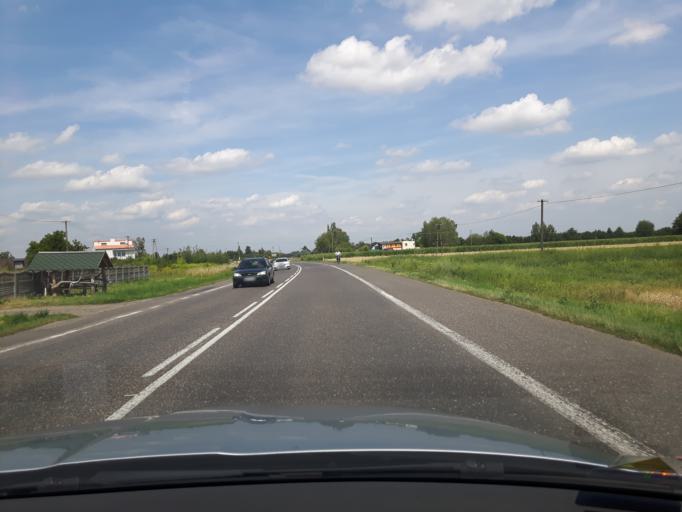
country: PL
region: Masovian Voivodeship
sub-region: Powiat plonski
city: Plonsk
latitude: 52.6517
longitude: 20.3776
